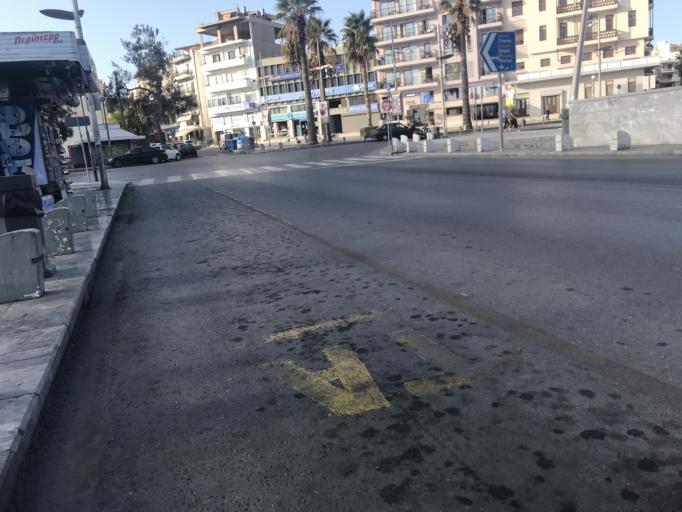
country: GR
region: Crete
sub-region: Nomos Irakleiou
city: Irakleion
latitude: 35.3375
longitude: 25.1369
